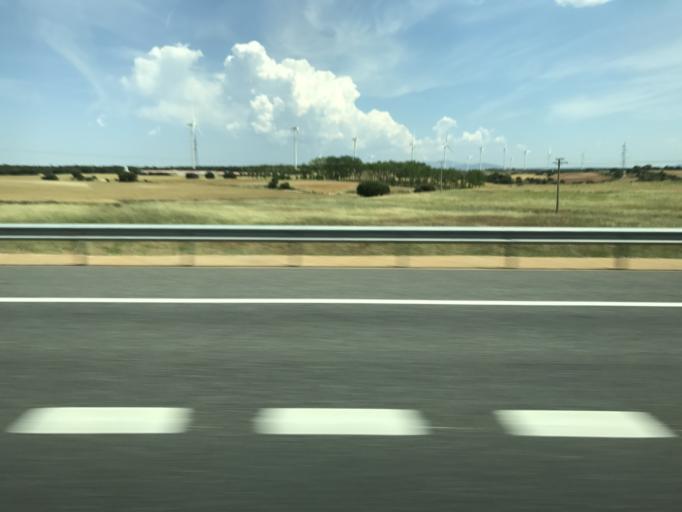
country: ES
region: Castille and Leon
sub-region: Provincia de Burgos
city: Cogollos
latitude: 42.2162
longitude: -3.7019
